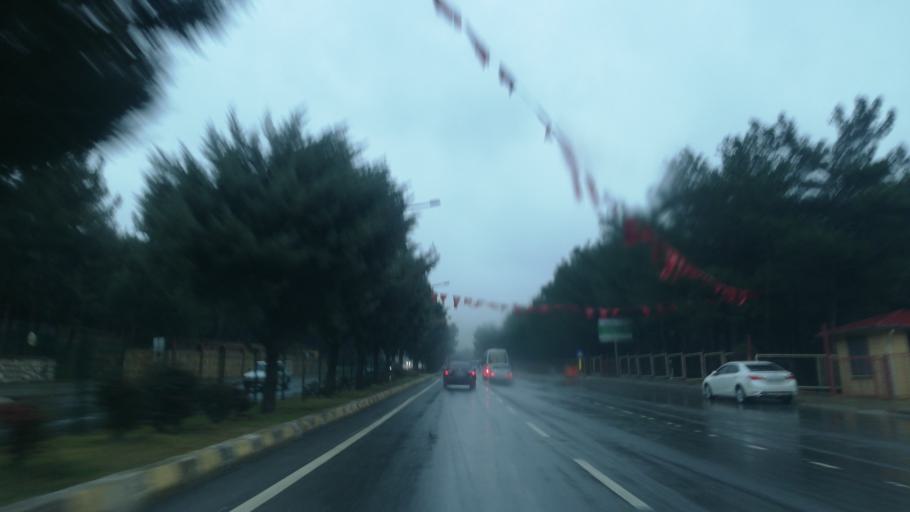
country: TR
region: Kahramanmaras
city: Kahramanmaras
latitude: 37.5981
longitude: 36.9200
